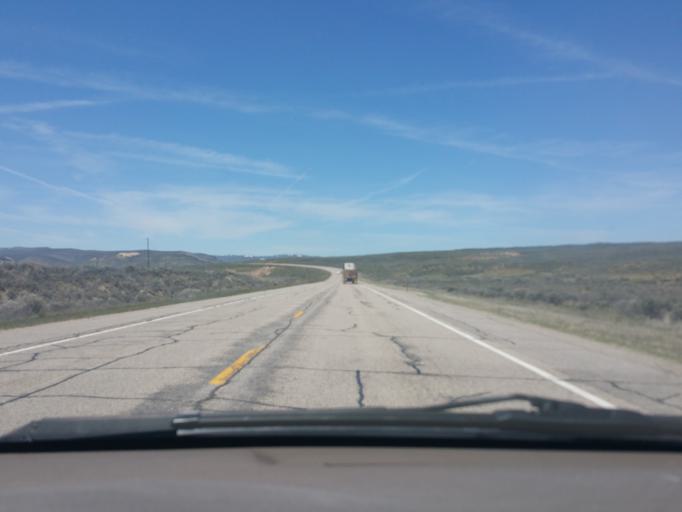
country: US
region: Wyoming
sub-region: Lincoln County
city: Kemmerer
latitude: 41.8158
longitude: -110.6562
